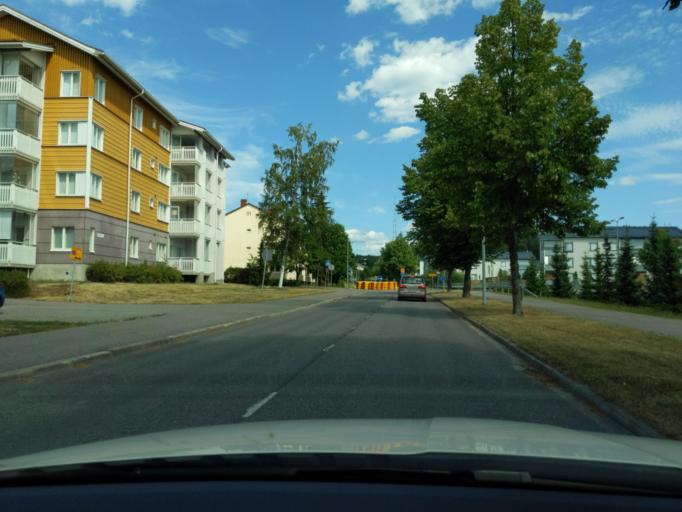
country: FI
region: Paijanne Tavastia
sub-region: Lahti
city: Lahti
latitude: 60.9709
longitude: 25.6353
